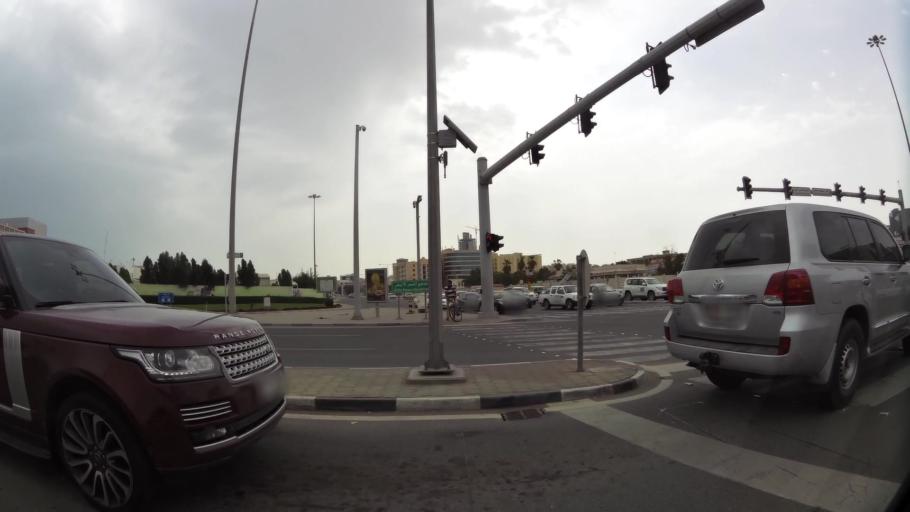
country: QA
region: Baladiyat ad Dawhah
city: Doha
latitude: 25.2907
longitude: 51.5070
